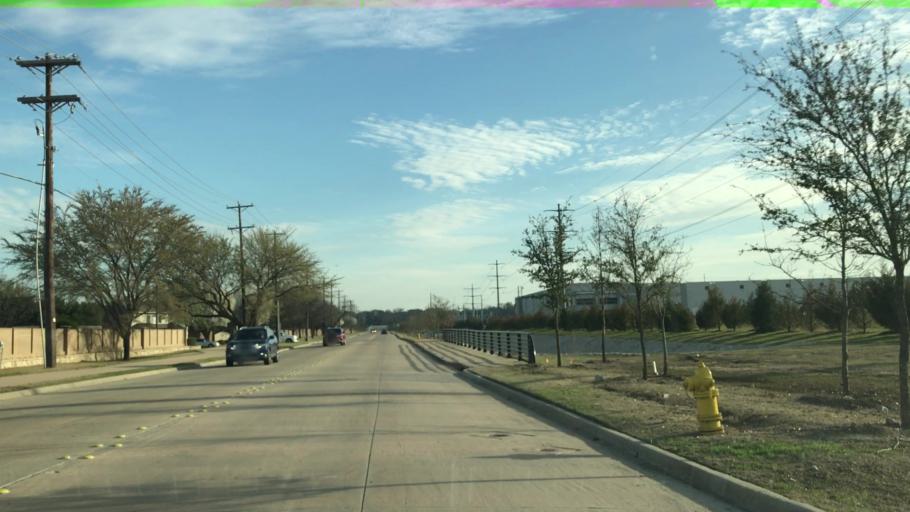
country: US
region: Texas
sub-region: Dallas County
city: Coppell
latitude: 32.9804
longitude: -97.0113
